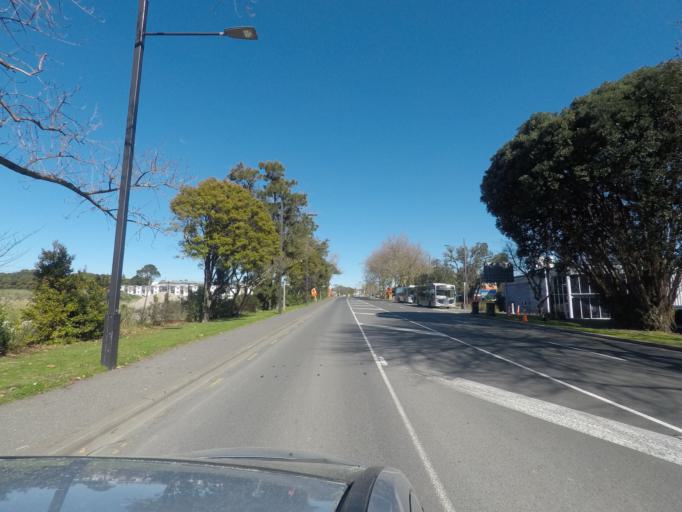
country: NZ
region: Auckland
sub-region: Auckland
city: Waitakere
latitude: -36.9108
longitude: 174.6829
